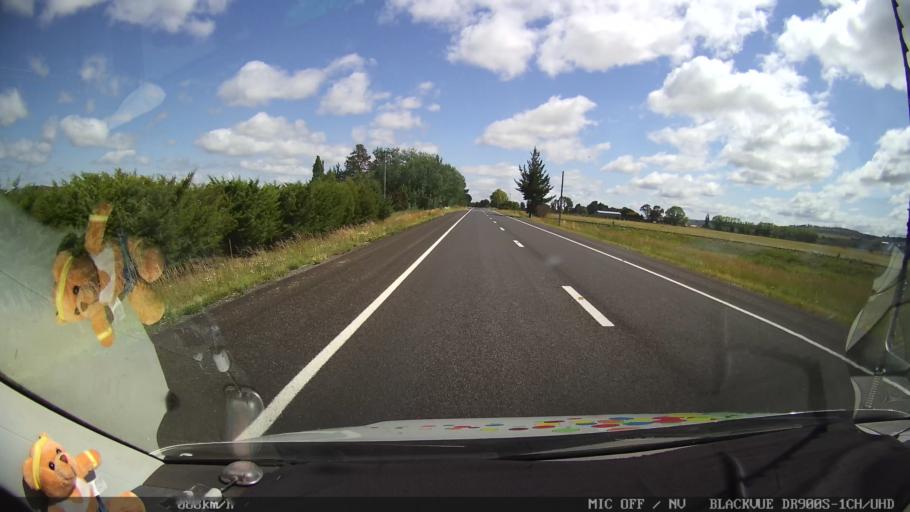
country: AU
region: New South Wales
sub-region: Glen Innes Severn
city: Glen Innes
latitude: -29.8234
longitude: 151.7395
